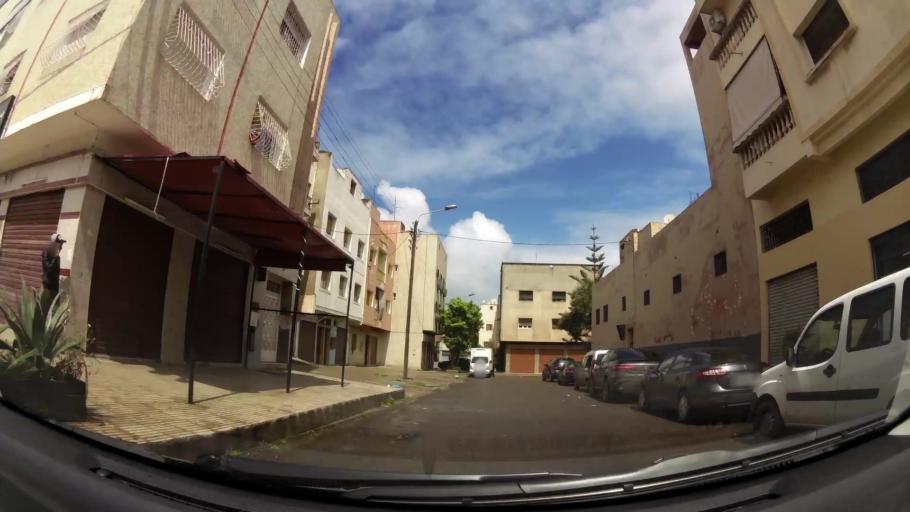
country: MA
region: Grand Casablanca
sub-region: Casablanca
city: Casablanca
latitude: 33.5514
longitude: -7.6787
